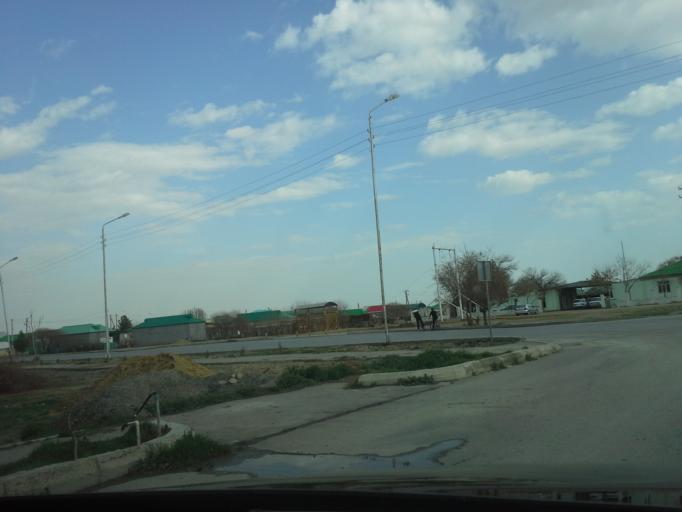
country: TM
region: Ahal
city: Ashgabat
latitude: 37.9897
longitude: 58.2873
